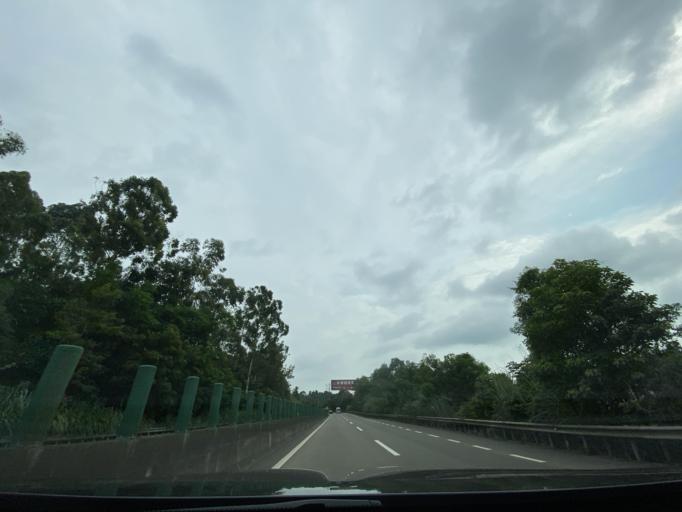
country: CN
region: Sichuan
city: Neijiang
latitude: 29.6363
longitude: 104.9838
